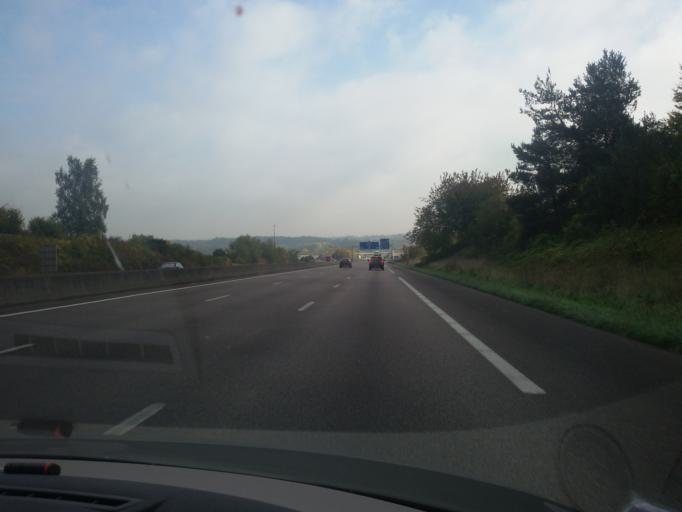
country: FR
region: Haute-Normandie
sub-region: Departement de l'Eure
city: Louviers
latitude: 49.2504
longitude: 1.1715
